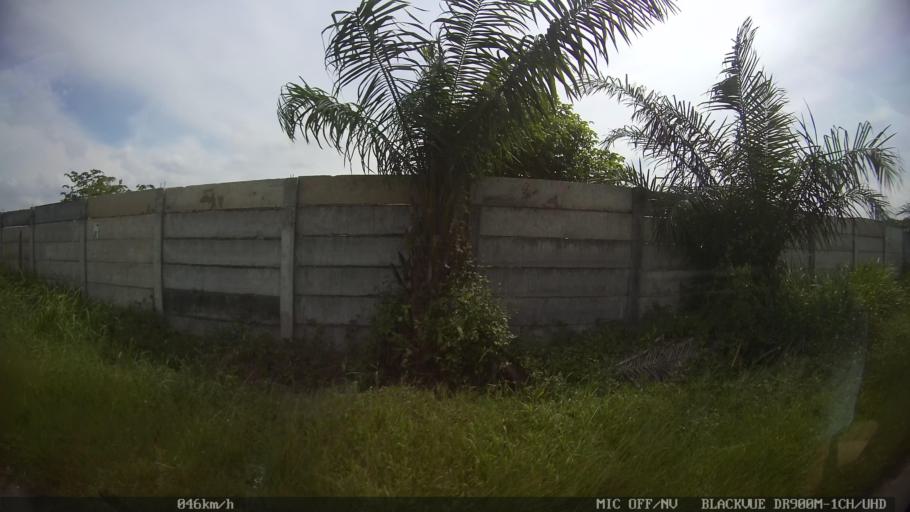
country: ID
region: North Sumatra
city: Percut
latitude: 3.6149
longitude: 98.8413
